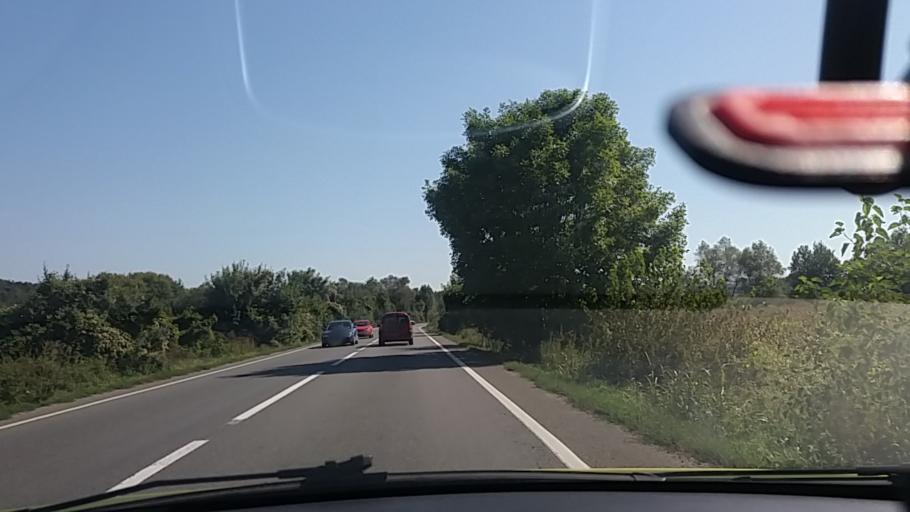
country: RO
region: Arad
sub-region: Comuna Barzava
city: Barzava
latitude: 46.1133
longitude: 21.9586
